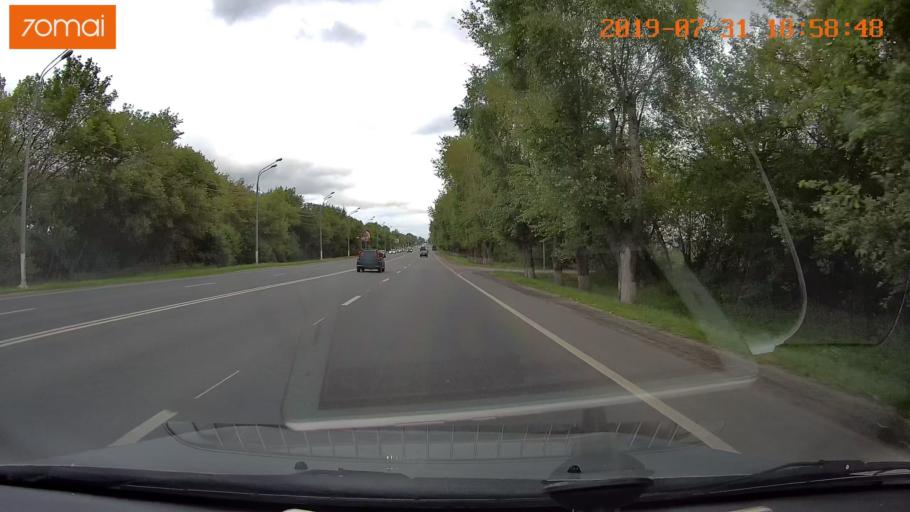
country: RU
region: Moskovskaya
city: Raduzhnyy
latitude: 55.1440
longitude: 38.7085
